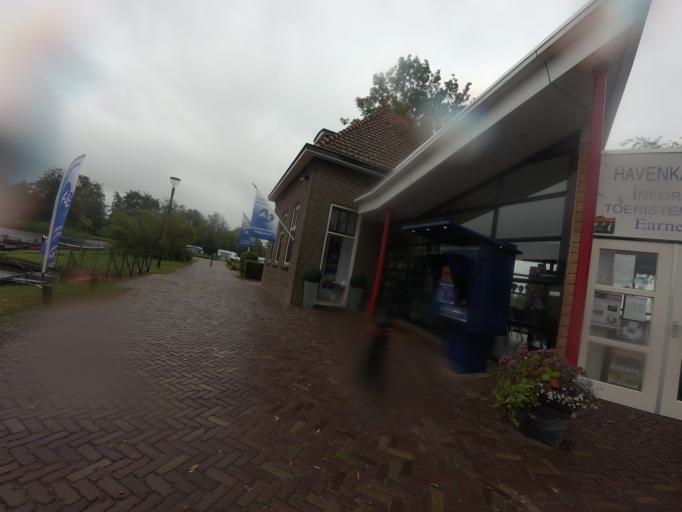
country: NL
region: Friesland
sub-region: Gemeente Boarnsterhim
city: Warten
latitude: 53.1289
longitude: 5.9382
